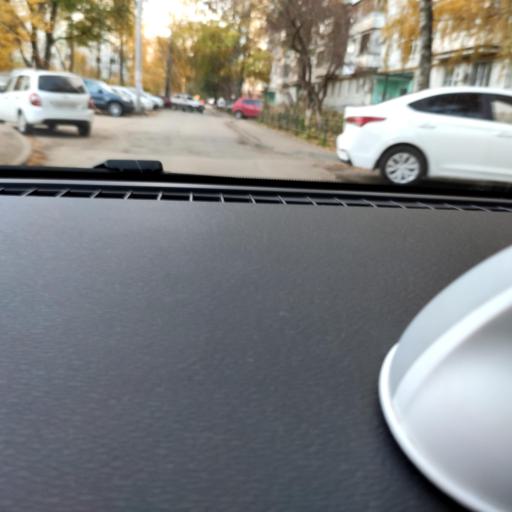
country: RU
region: Samara
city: Samara
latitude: 53.2416
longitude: 50.2131
